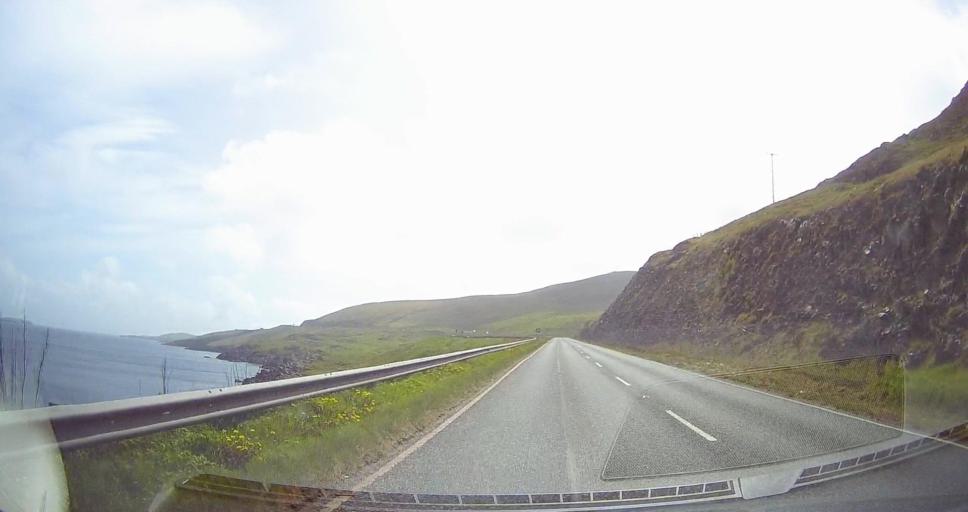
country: GB
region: Scotland
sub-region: Shetland Islands
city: Sandwick
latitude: 60.0319
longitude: -1.2339
